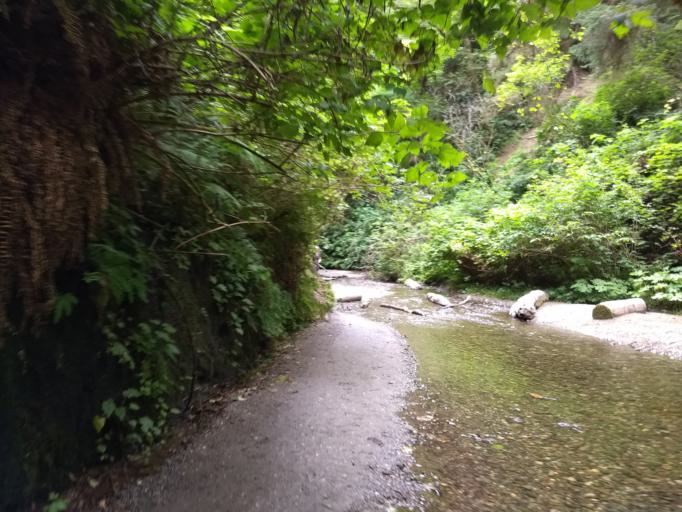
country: US
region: California
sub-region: Humboldt County
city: Westhaven-Moonstone
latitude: 41.4033
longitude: -124.0631
